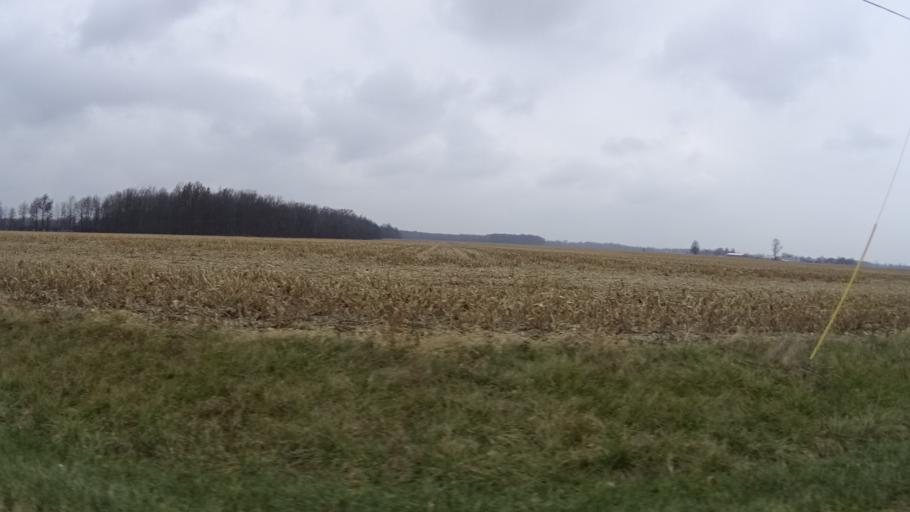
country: US
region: Ohio
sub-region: Lorain County
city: Oberlin
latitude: 41.3378
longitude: -82.2050
